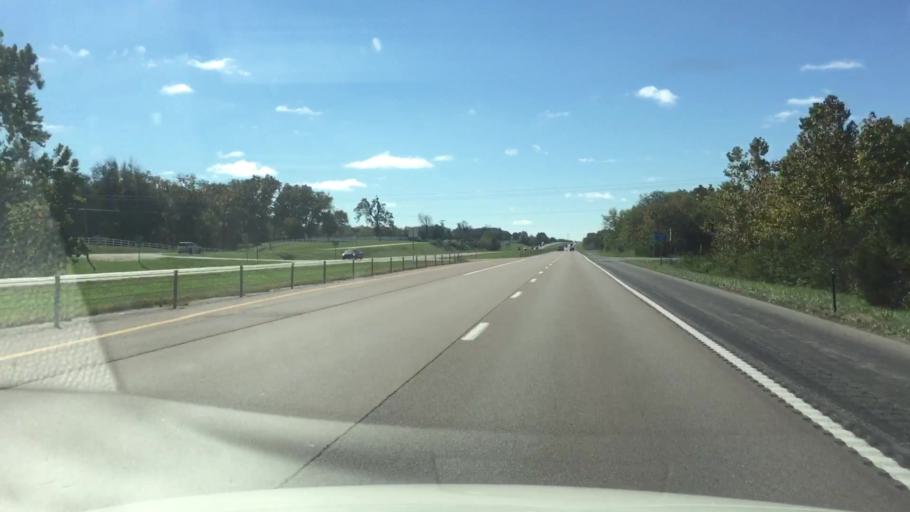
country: US
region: Missouri
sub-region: Boone County
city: Ashland
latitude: 38.8115
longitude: -92.2515
